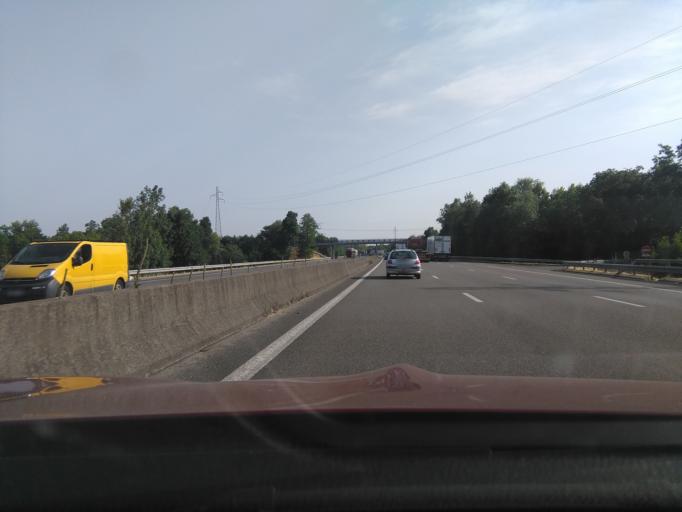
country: FR
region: Bourgogne
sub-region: Departement de Saone-et-Loire
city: La Chapelle-de-Guinchay
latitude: 46.1861
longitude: 4.7723
